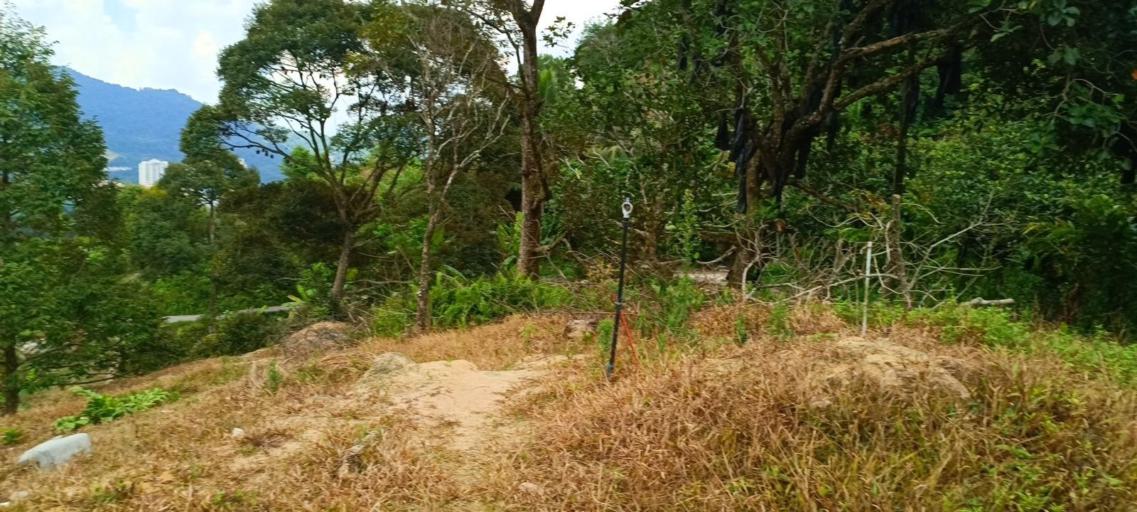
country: MY
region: Penang
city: Kampung Sungai Ara
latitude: 5.3343
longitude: 100.2544
